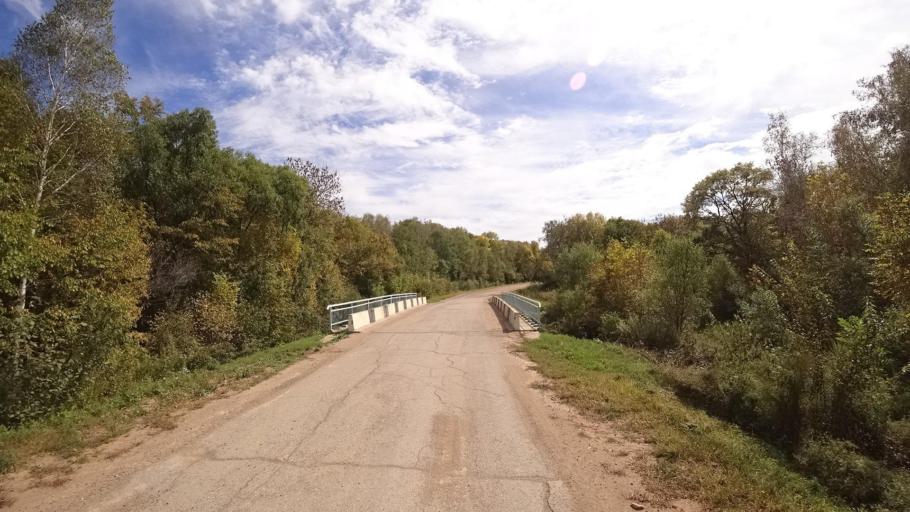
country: RU
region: Primorskiy
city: Yakovlevka
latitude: 44.6351
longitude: 133.5992
